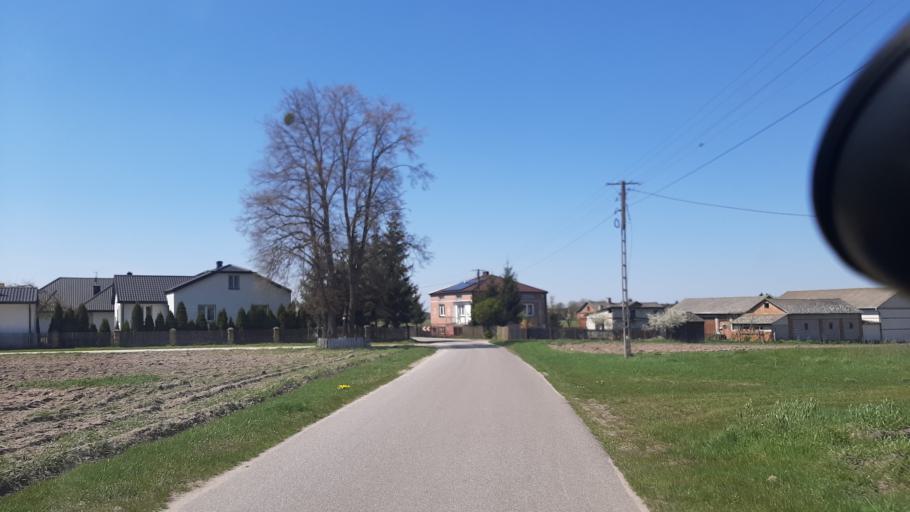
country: PL
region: Lublin Voivodeship
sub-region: Powiat lubelski
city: Garbow
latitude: 51.4026
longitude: 22.3261
